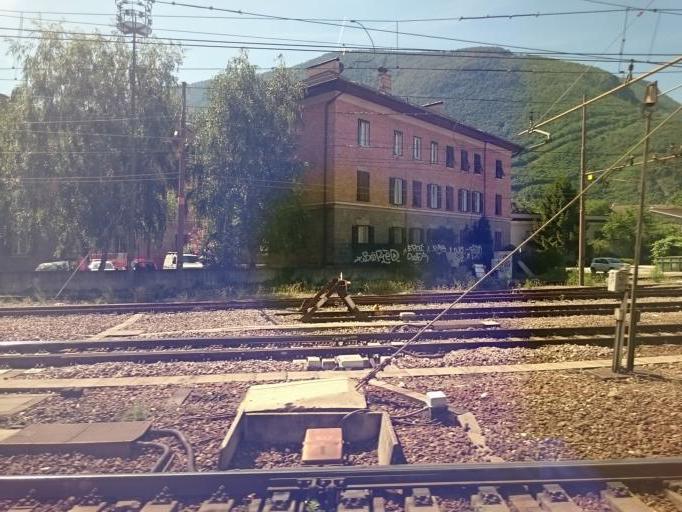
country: IT
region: Trentino-Alto Adige
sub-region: Bolzano
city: Bolzano
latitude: 46.4992
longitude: 11.3643
